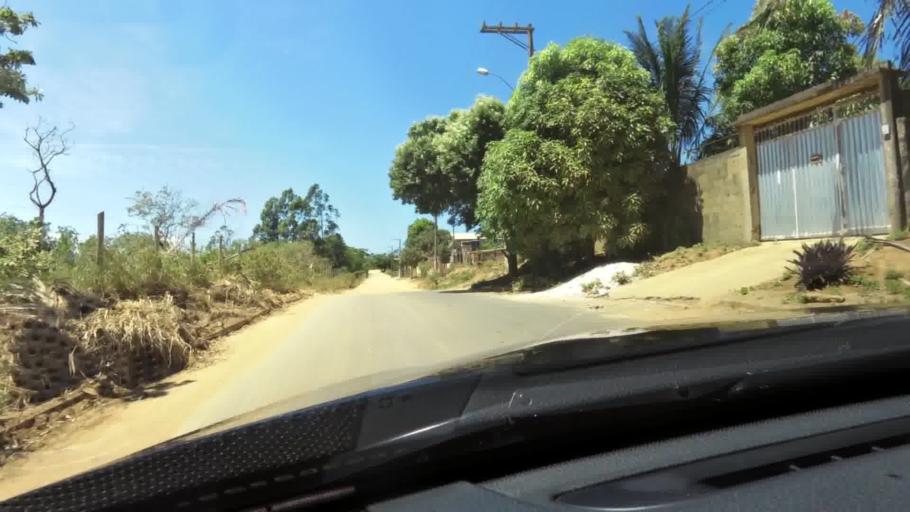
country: BR
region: Espirito Santo
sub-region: Guarapari
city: Guarapari
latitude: -20.6174
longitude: -40.4645
